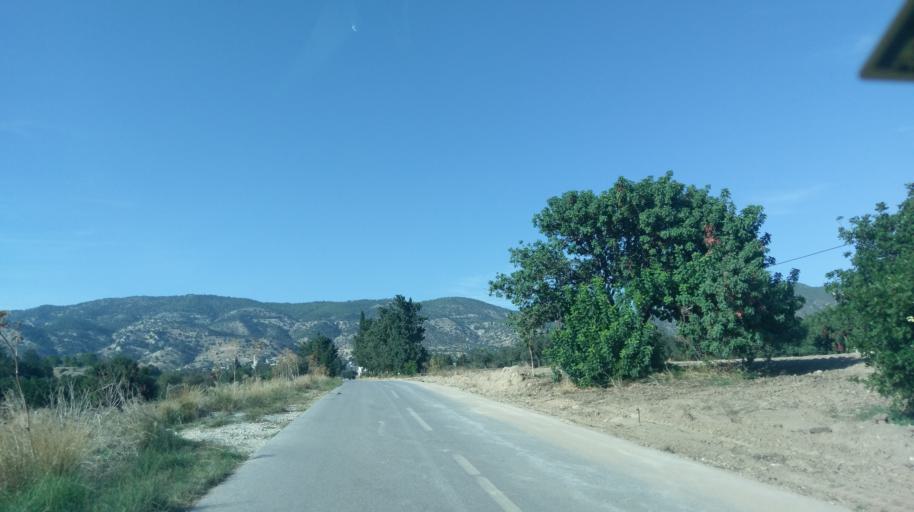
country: CY
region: Ammochostos
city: Trikomo
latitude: 35.3337
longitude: 33.8096
